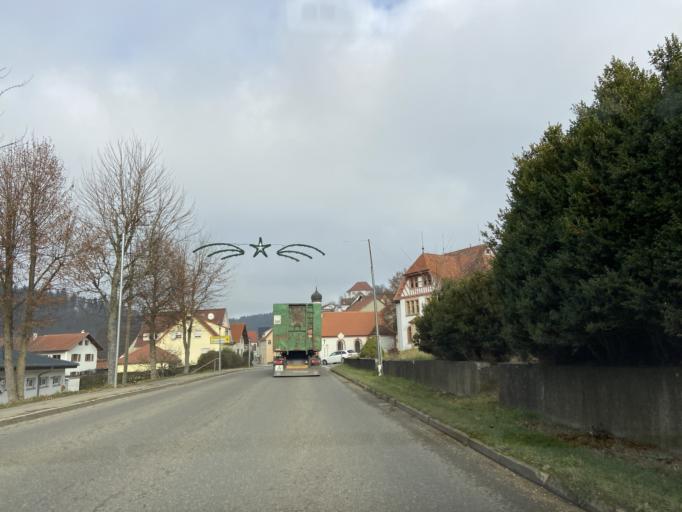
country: DE
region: Baden-Wuerttemberg
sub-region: Tuebingen Region
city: Hettingen
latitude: 48.2136
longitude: 9.2308
